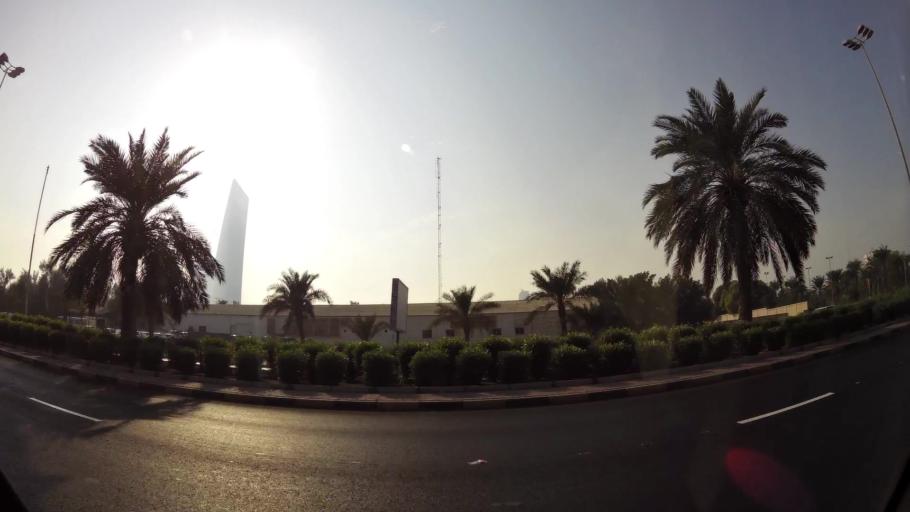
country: KW
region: Al Asimah
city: Ad Dasmah
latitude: 29.3852
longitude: 48.0025
